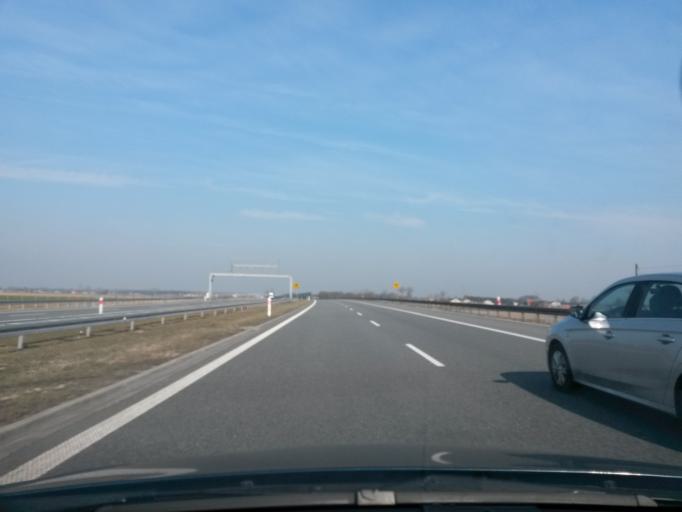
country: PL
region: Lodz Voivodeship
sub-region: Powiat leczycki
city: Piatek
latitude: 52.0753
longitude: 19.5332
